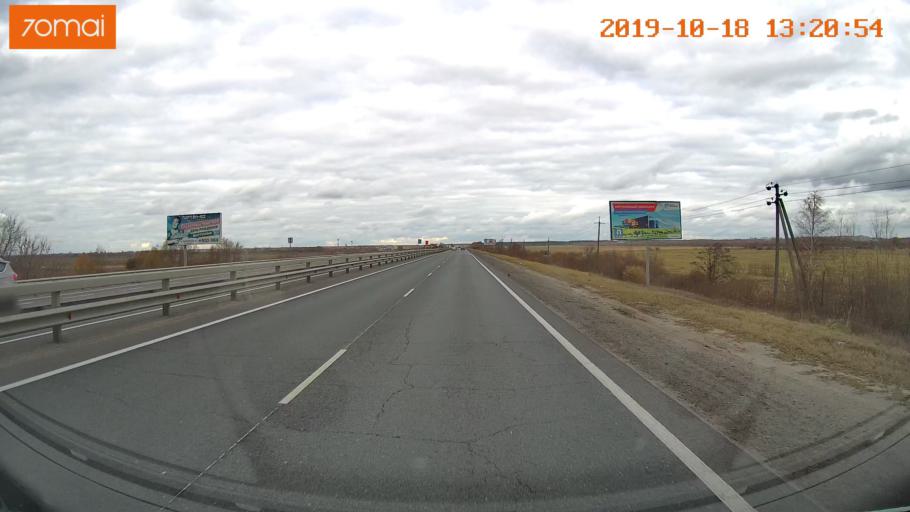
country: RU
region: Rjazan
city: Polyany
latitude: 54.6875
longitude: 39.8354
